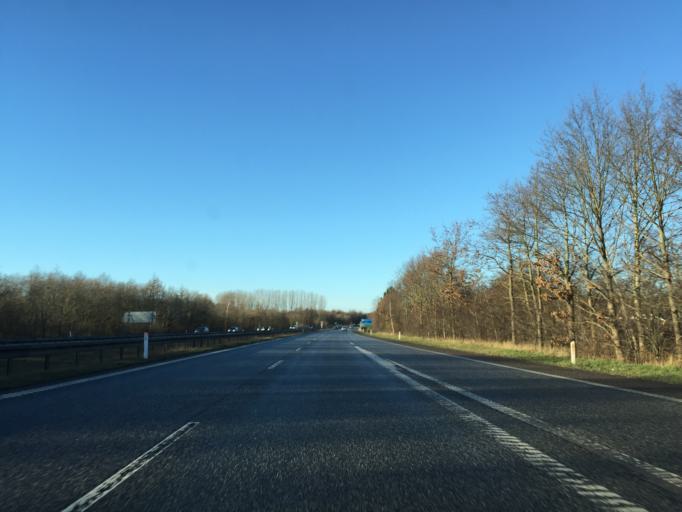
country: DK
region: South Denmark
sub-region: Odense Kommune
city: Odense
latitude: 55.3542
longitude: 10.3690
